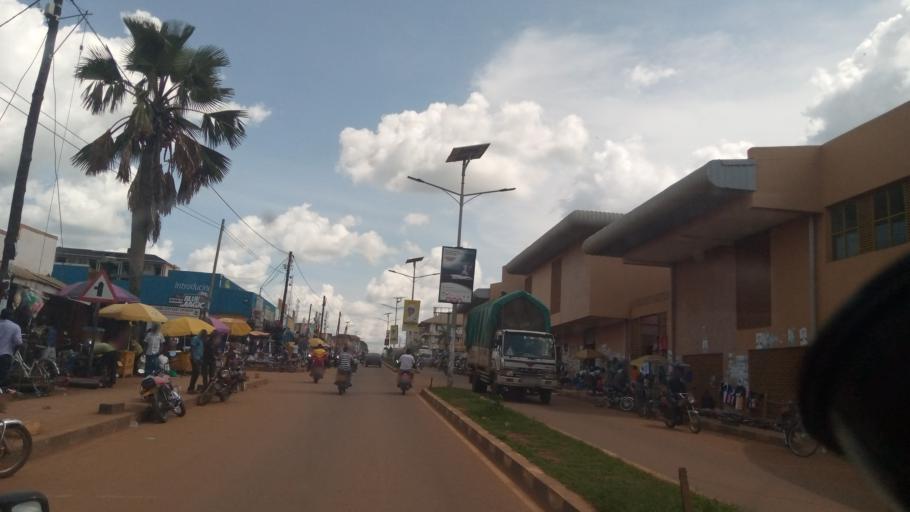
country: UG
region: Northern Region
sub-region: Lira District
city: Lira
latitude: 2.2440
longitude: 32.8978
